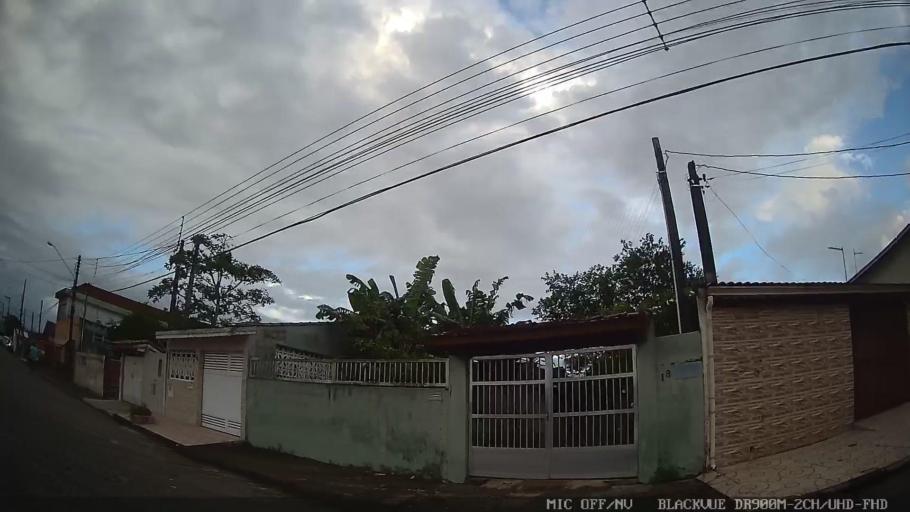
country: BR
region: Sao Paulo
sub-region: Itanhaem
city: Itanhaem
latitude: -24.1762
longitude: -46.7883
